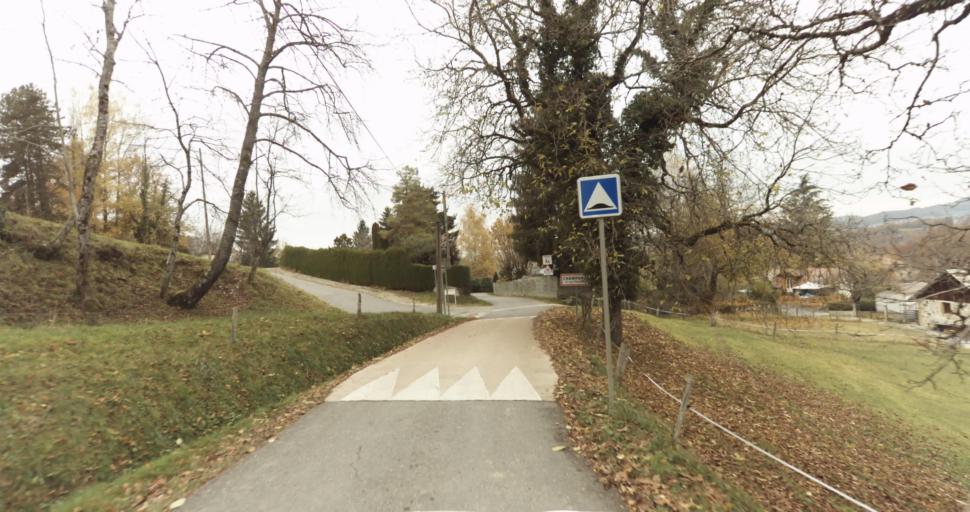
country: FR
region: Rhone-Alpes
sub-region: Departement de la Haute-Savoie
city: Chavanod
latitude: 45.8745
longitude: 6.0360
